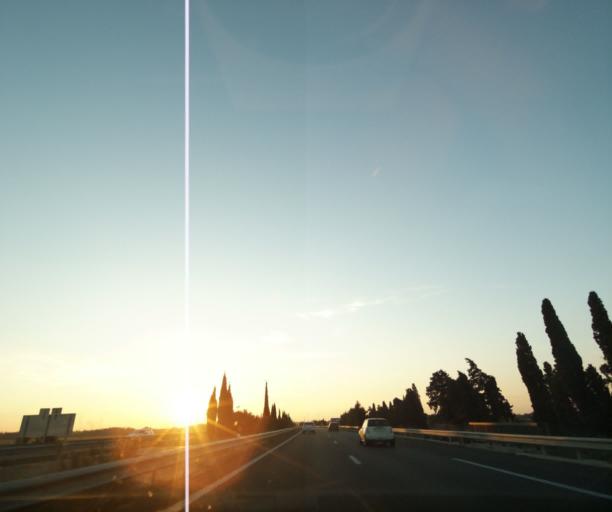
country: FR
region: Provence-Alpes-Cote d'Azur
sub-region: Departement des Bouches-du-Rhone
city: Mouries
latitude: 43.6393
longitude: 4.8714
